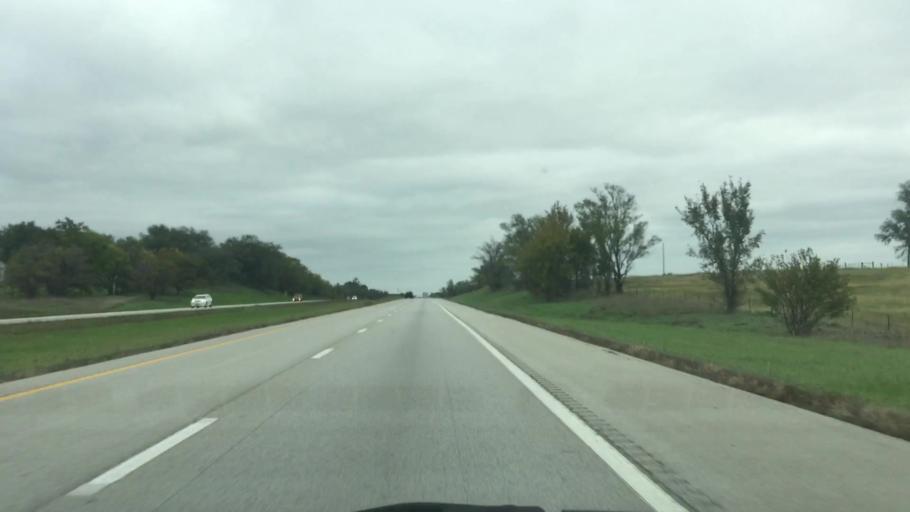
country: US
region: Missouri
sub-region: Clinton County
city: Cameron
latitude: 39.7845
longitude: -94.2069
